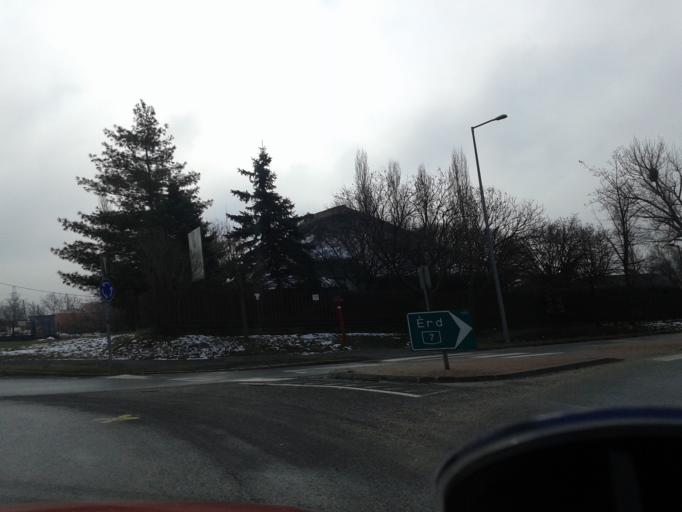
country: HU
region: Pest
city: Diosd
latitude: 47.4041
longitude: 18.9455
